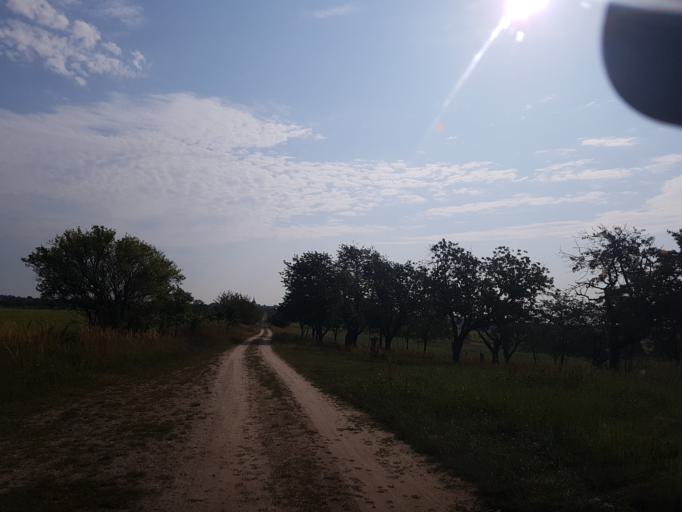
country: DE
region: Brandenburg
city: Hohenleipisch
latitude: 51.4972
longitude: 13.5328
